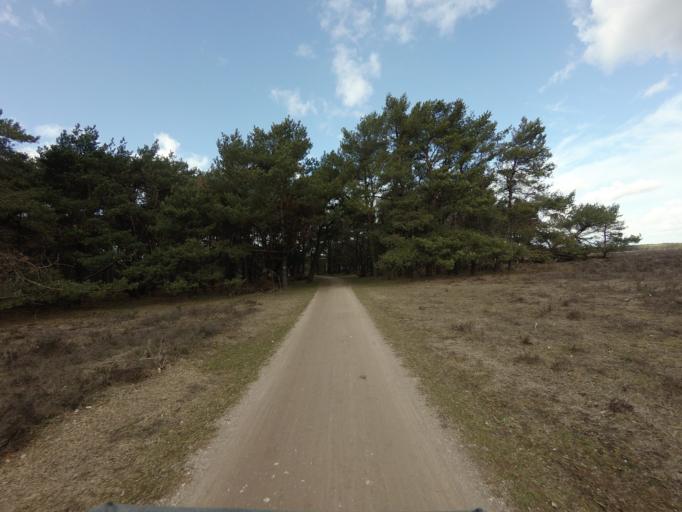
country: NL
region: North Holland
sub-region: Gemeente Bussum
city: Bussum
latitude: 52.2554
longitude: 5.1751
